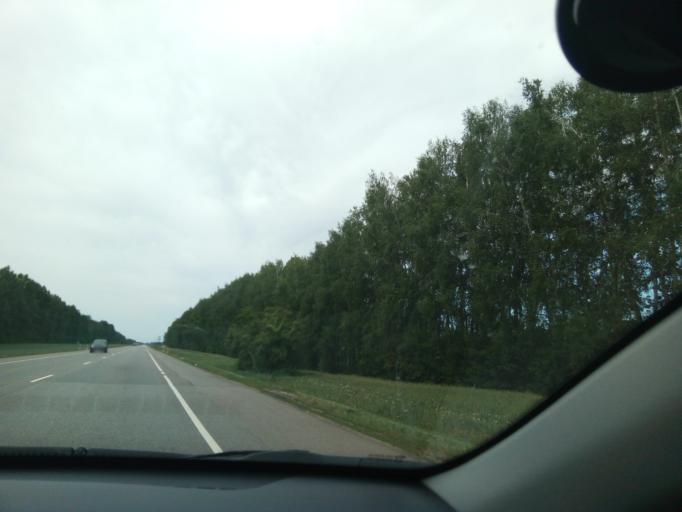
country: RU
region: Tambov
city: Selezni
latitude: 52.6672
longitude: 41.0966
